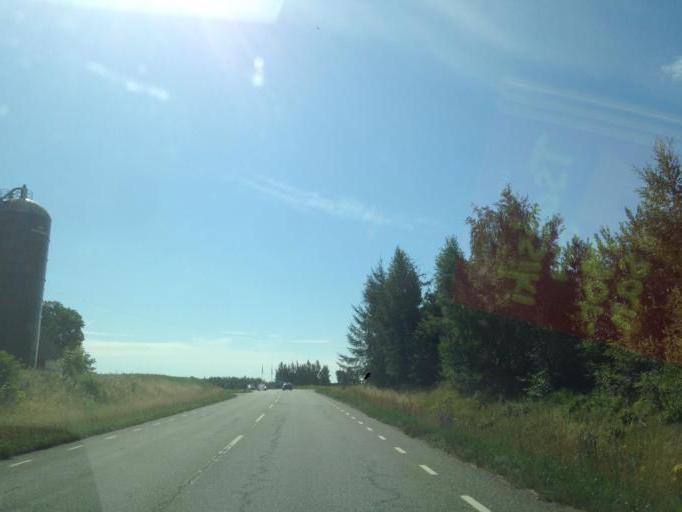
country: SE
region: Skane
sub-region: Simrishamns Kommun
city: Kivik
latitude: 55.6259
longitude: 14.2584
